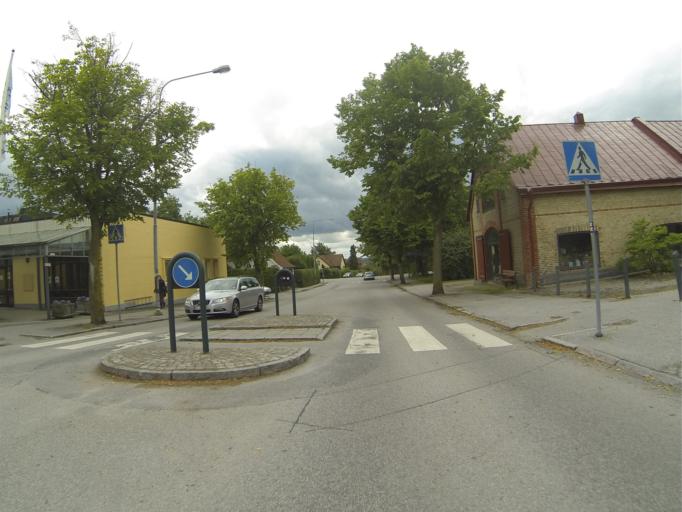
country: SE
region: Skane
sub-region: Lunds Kommun
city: Genarp
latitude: 55.6644
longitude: 13.3476
